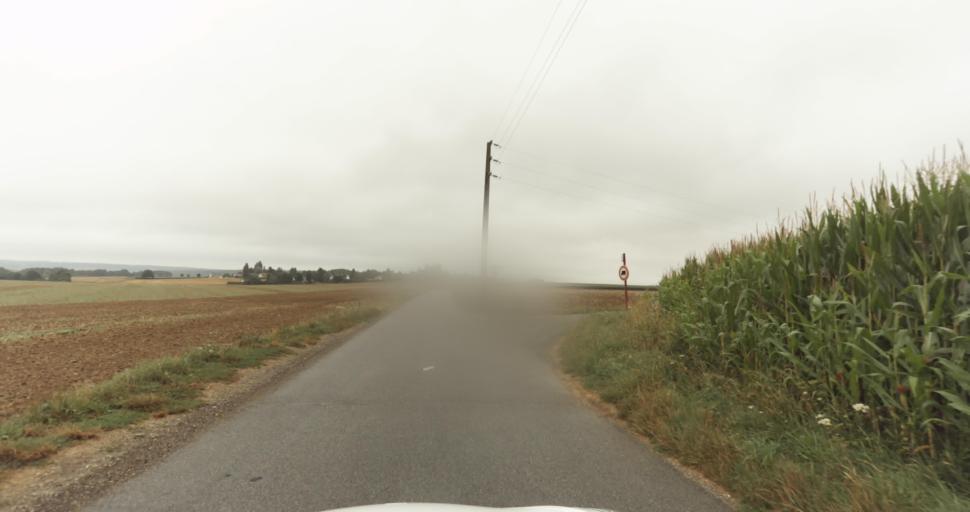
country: FR
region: Haute-Normandie
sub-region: Departement de l'Eure
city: Normanville
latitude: 49.0806
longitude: 1.1949
